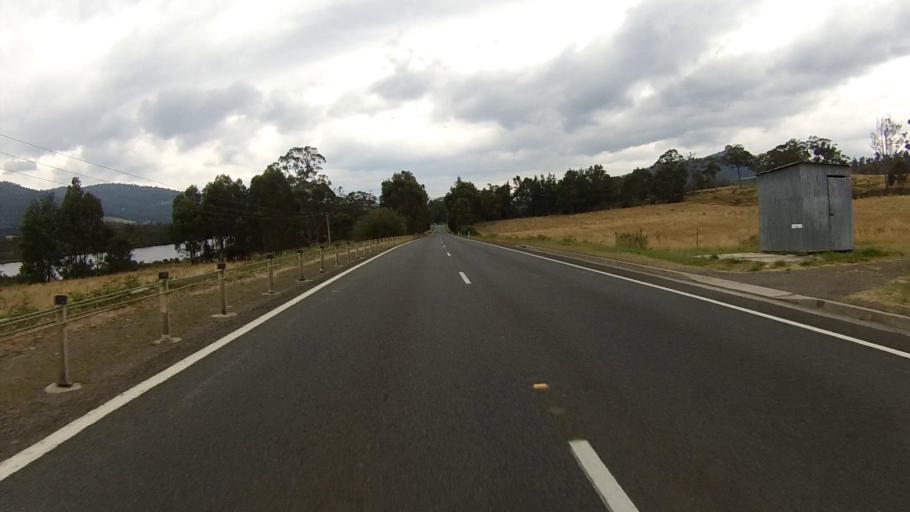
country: AU
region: Tasmania
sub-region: Huon Valley
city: Franklin
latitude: -43.0829
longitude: 147.0307
